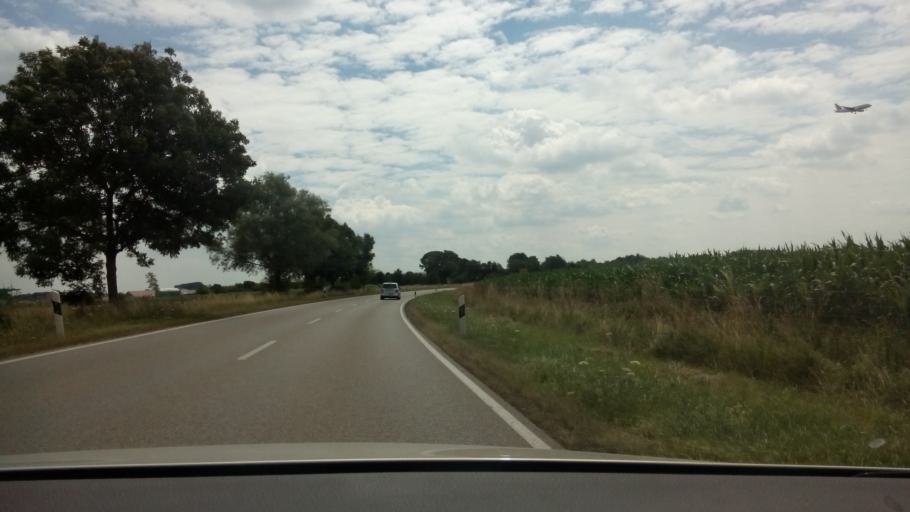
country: DE
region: Bavaria
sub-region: Upper Bavaria
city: Eitting
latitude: 48.3755
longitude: 11.8483
